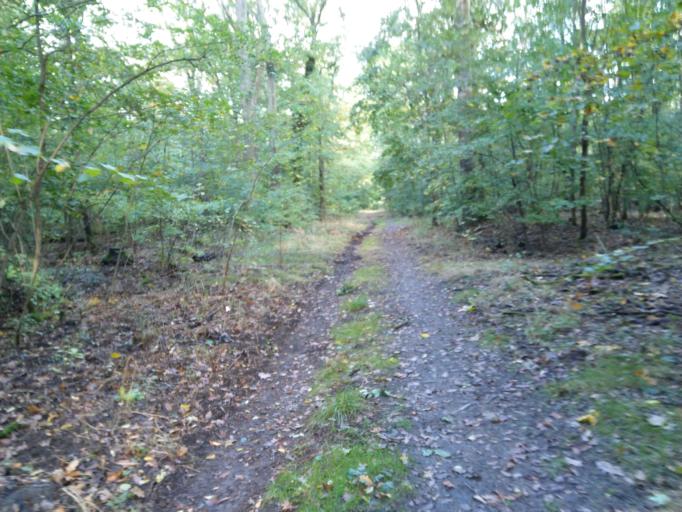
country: DE
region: Berlin
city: Rahnsdorf
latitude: 52.4502
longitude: 13.6858
